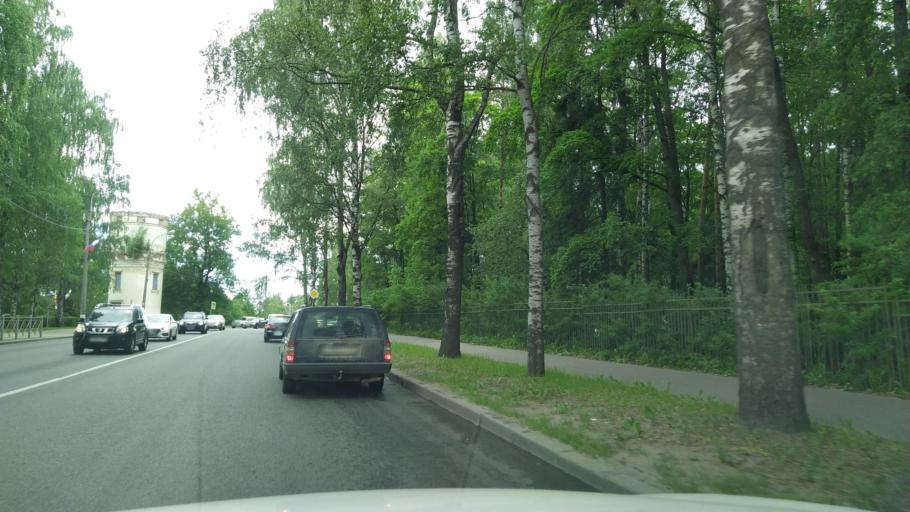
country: RU
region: St.-Petersburg
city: Pavlovsk
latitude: 59.6906
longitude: 30.4332
